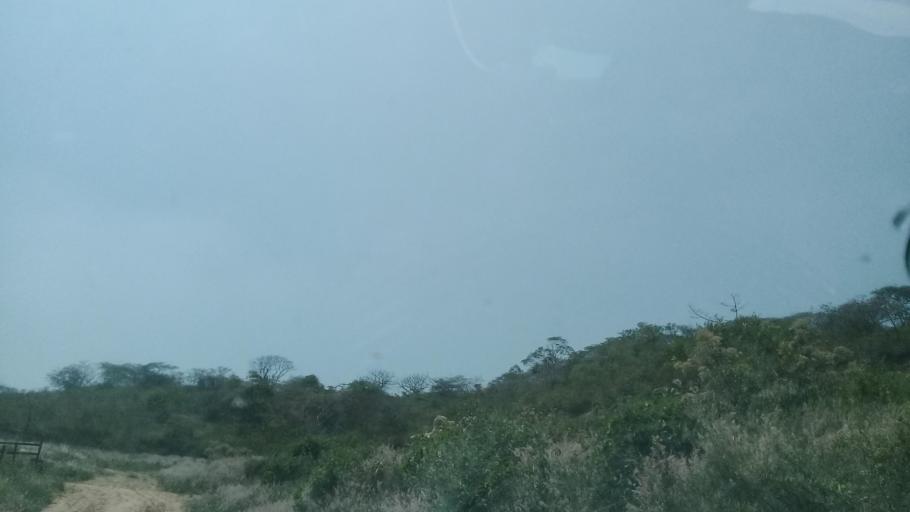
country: MX
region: Veracruz
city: El Castillo
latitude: 19.5557
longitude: -96.8583
